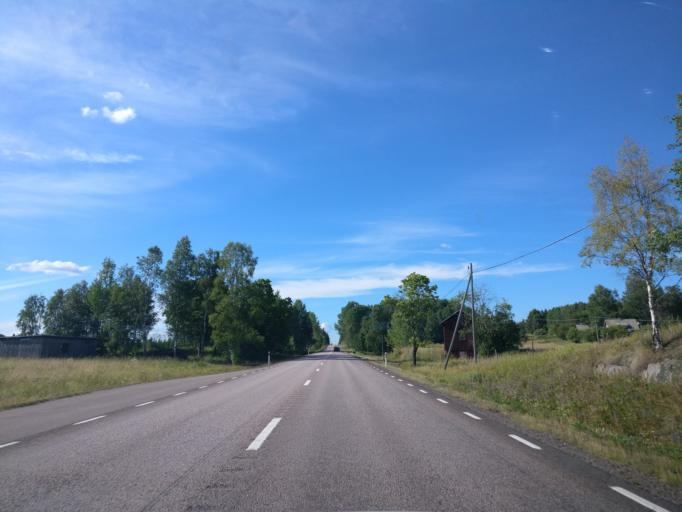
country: SE
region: Vaermland
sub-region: Karlstads Kommun
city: Edsvalla
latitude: 59.5807
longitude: 13.0168
